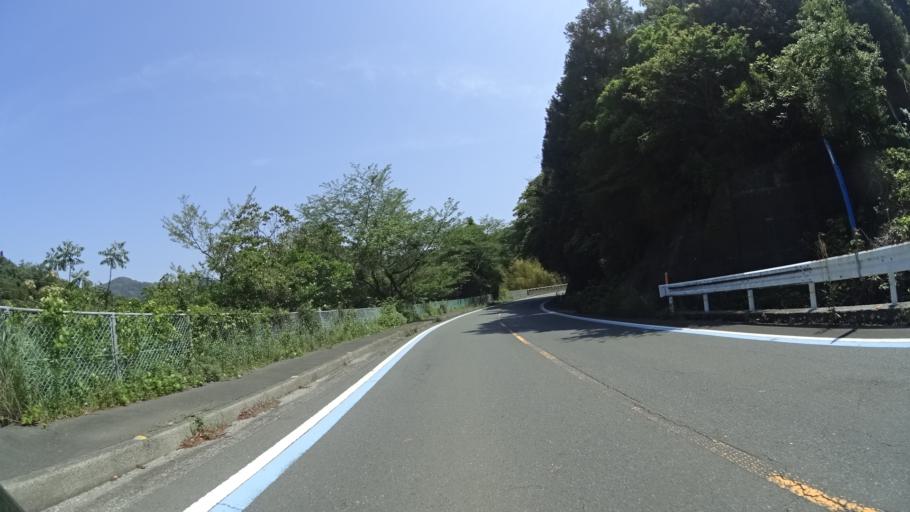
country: JP
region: Ehime
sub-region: Nishiuwa-gun
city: Ikata-cho
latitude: 33.3959
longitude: 132.1429
